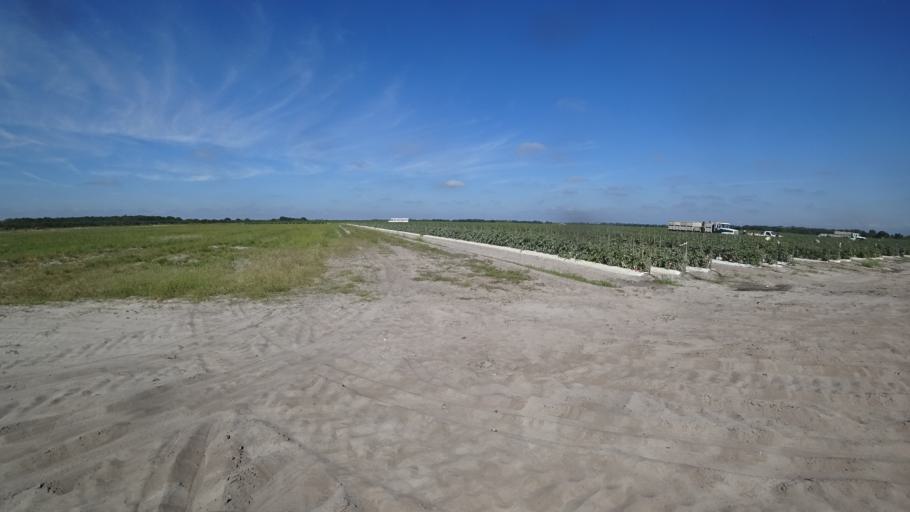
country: US
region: Florida
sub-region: DeSoto County
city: Arcadia
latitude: 27.2966
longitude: -82.0510
